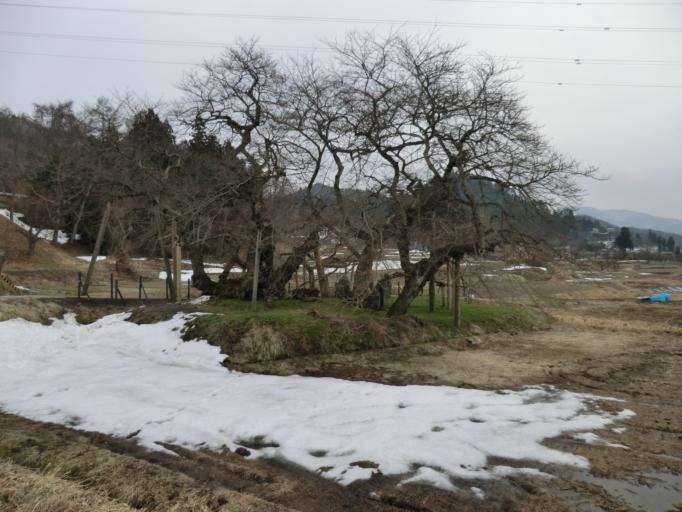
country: JP
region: Fukushima
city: Kitakata
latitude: 37.5104
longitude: 139.9541
